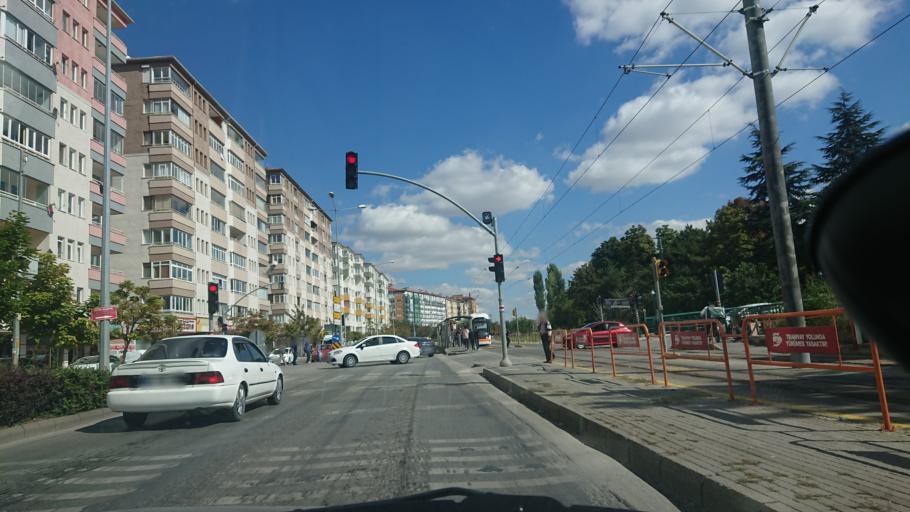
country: TR
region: Eskisehir
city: Eskisehir
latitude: 39.7674
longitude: 30.5426
